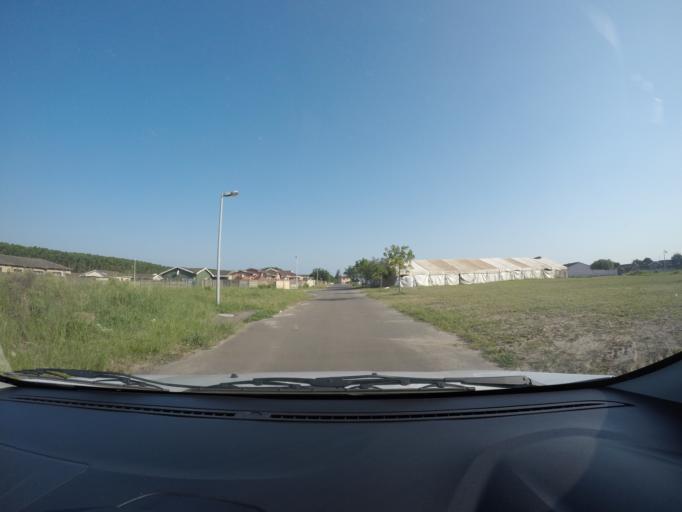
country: ZA
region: KwaZulu-Natal
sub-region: uThungulu District Municipality
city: Richards Bay
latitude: -28.7103
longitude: 32.0383
